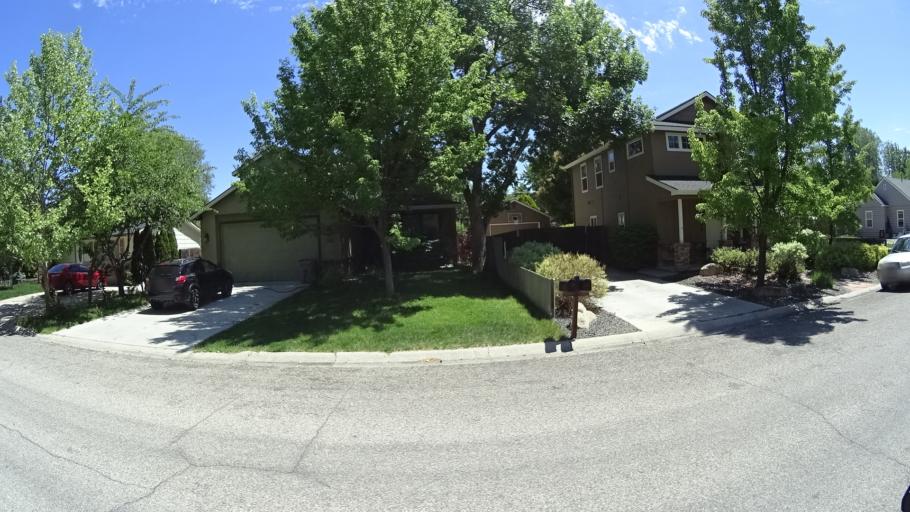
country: US
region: Idaho
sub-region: Ada County
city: Boise
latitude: 43.6025
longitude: -116.2236
